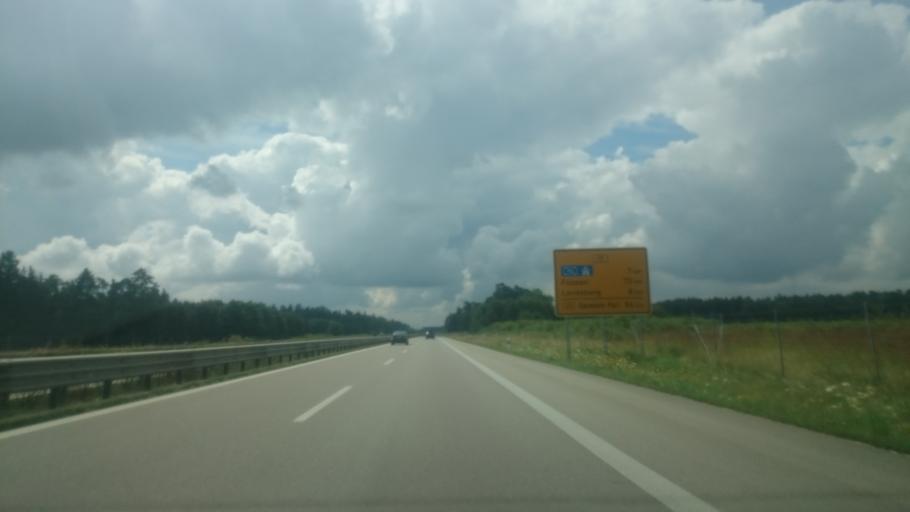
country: DE
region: Bavaria
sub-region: Upper Bavaria
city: Hurlach
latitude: 48.1062
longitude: 10.8361
